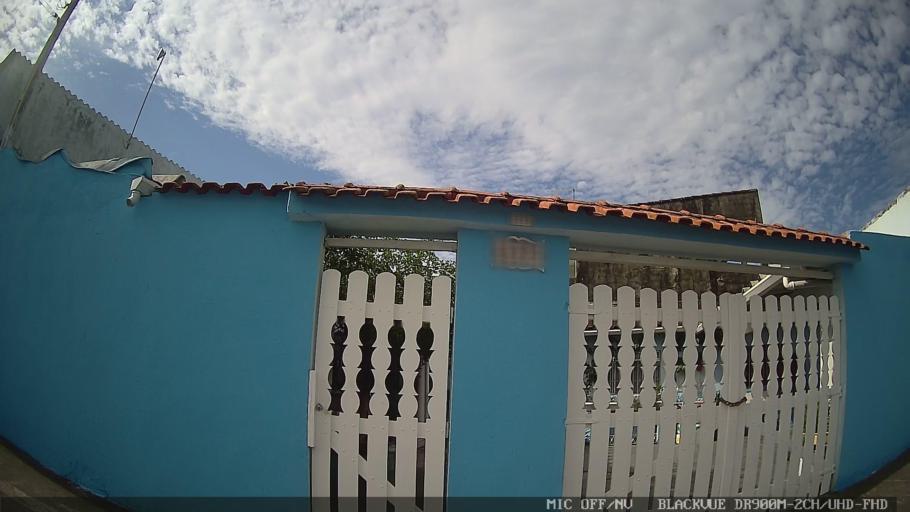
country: BR
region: Sao Paulo
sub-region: Itanhaem
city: Itanhaem
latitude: -24.1613
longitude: -46.7648
